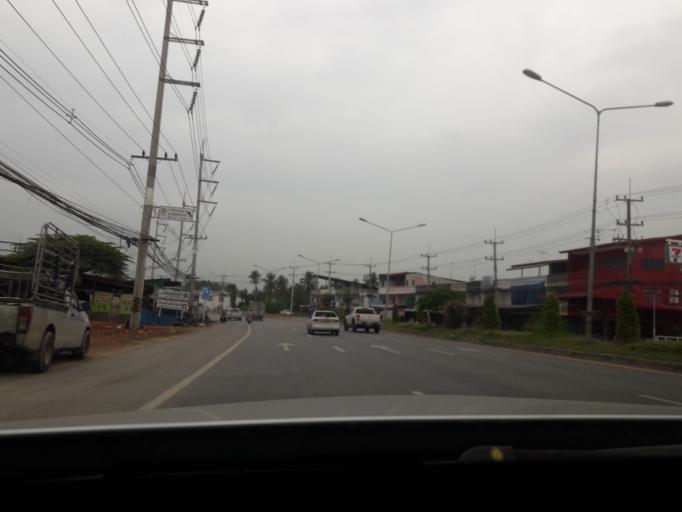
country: TH
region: Samut Songkhram
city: Samut Songkhram
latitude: 13.4220
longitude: 99.9877
